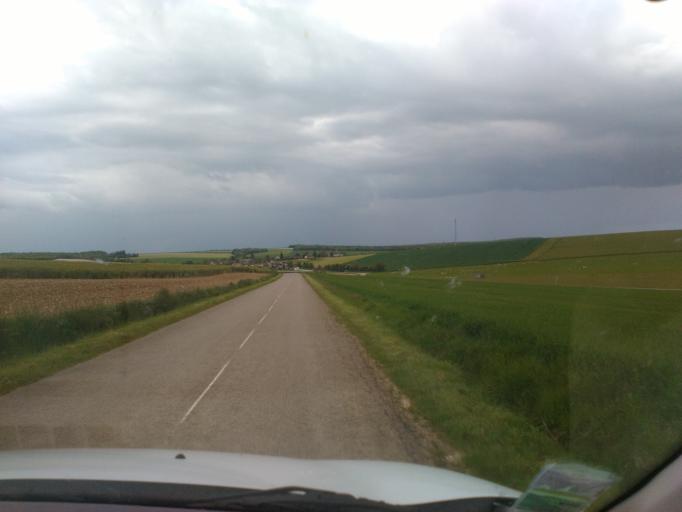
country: FR
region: Bourgogne
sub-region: Departement de l'Yonne
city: Thorigny-sur-Oreuse
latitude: 48.3600
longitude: 3.4441
